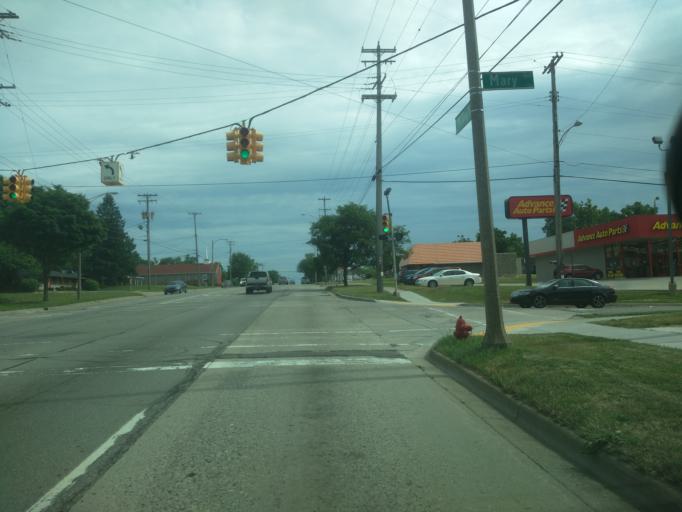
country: US
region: Michigan
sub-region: Ingham County
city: Lansing
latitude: 42.6914
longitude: -84.5677
